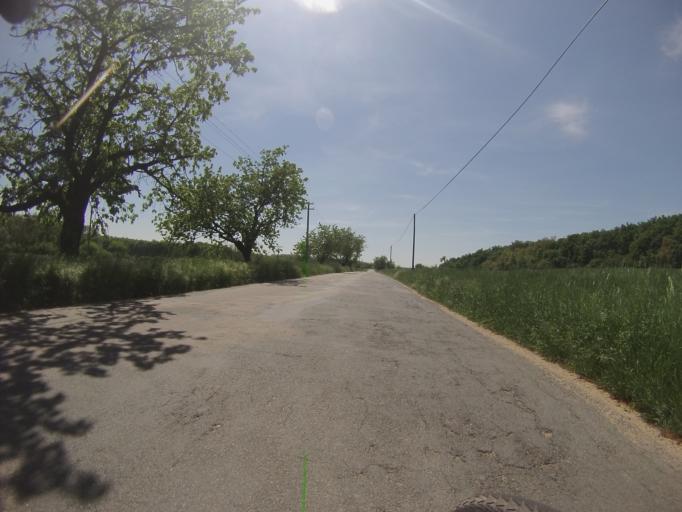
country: CZ
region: South Moravian
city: Vranovice
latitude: 48.9558
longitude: 16.6009
